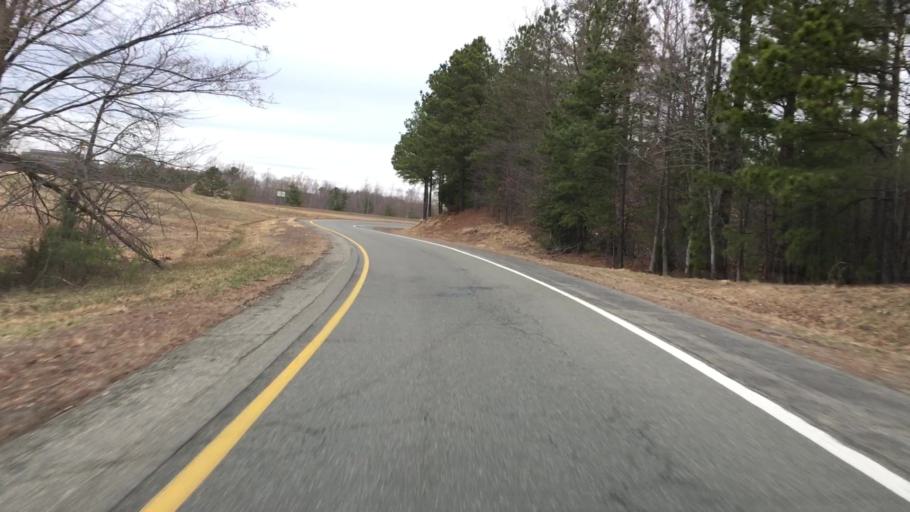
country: US
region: Virginia
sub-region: Henrico County
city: Short Pump
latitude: 37.6362
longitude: -77.5718
